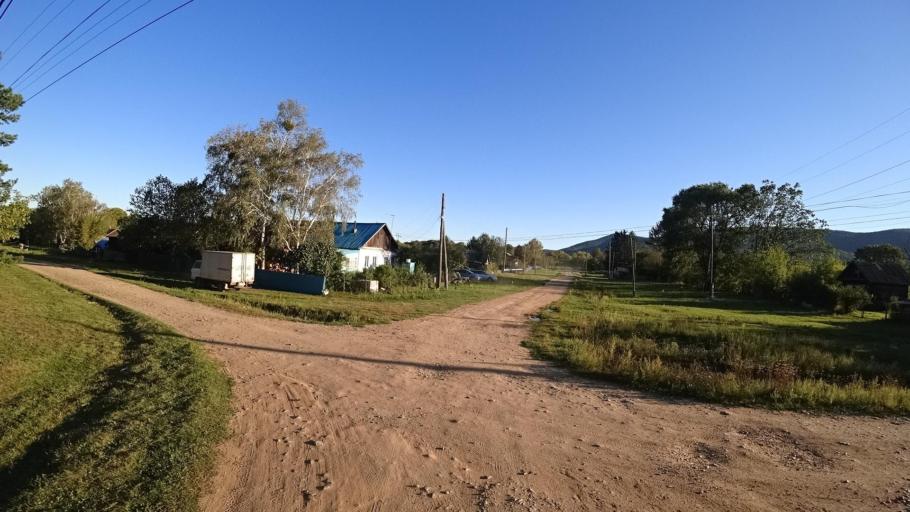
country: RU
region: Primorskiy
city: Kirovskiy
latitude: 44.8321
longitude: 133.5729
